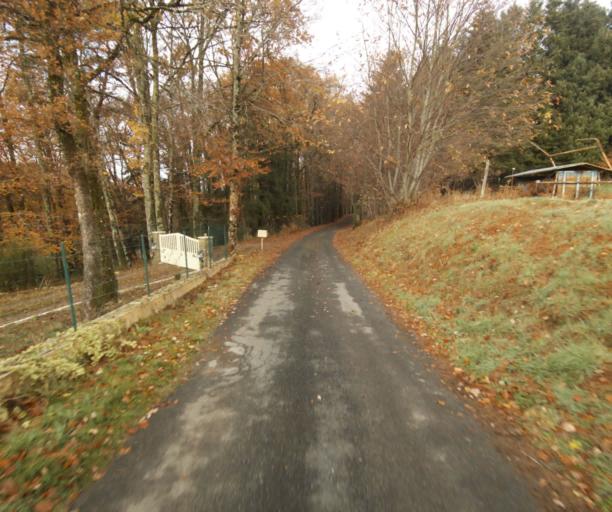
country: FR
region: Limousin
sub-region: Departement de la Correze
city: Cornil
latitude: 45.2000
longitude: 1.7120
